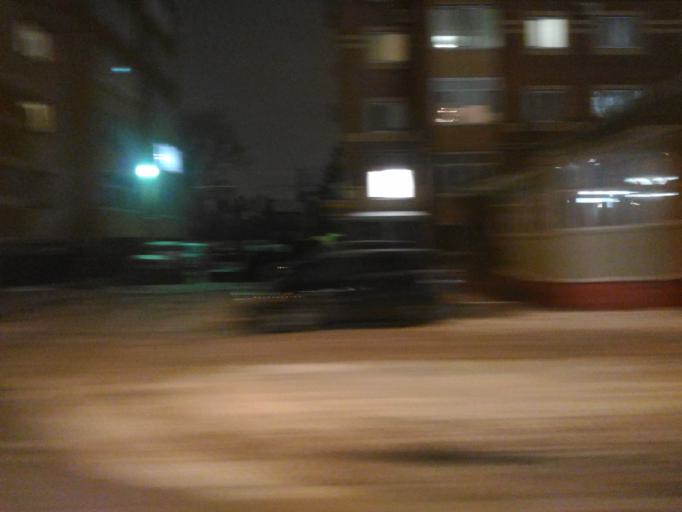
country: RU
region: Ulyanovsk
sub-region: Ulyanovskiy Rayon
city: Ulyanovsk
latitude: 54.3262
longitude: 48.4034
